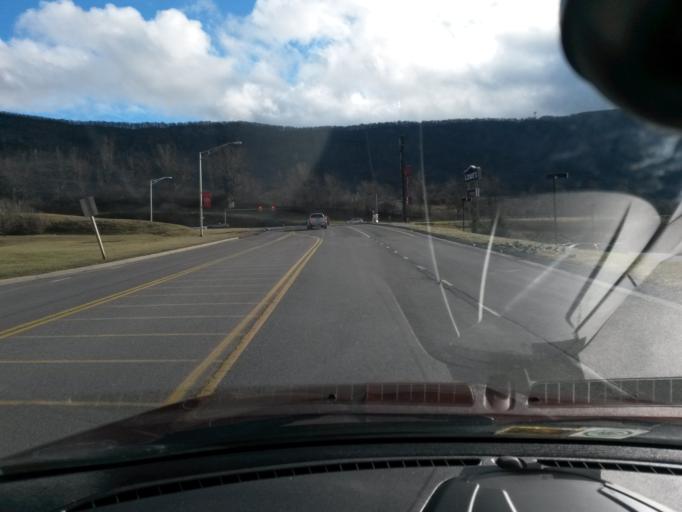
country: US
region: Virginia
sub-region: Tazewell County
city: Bluefield
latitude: 37.2388
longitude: -81.2491
